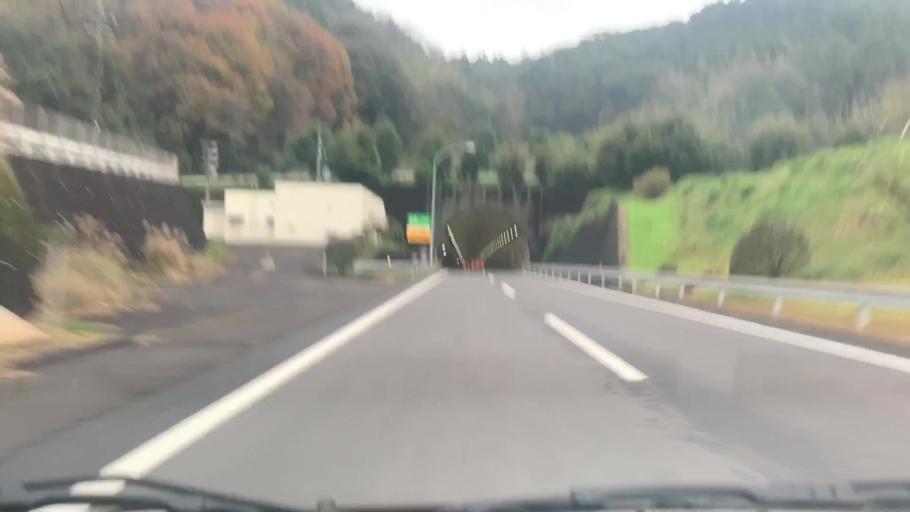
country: JP
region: Nagasaki
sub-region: Isahaya-shi
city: Isahaya
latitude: 32.8740
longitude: 129.9980
